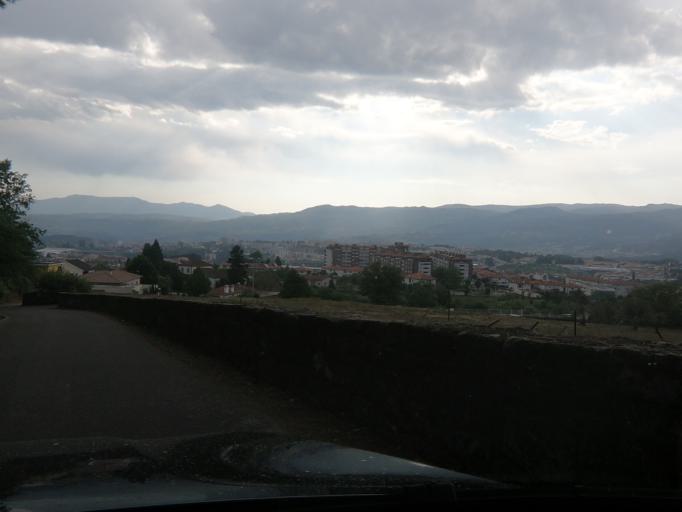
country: PT
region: Vila Real
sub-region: Vila Real
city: Vila Real
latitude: 41.3059
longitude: -7.7165
